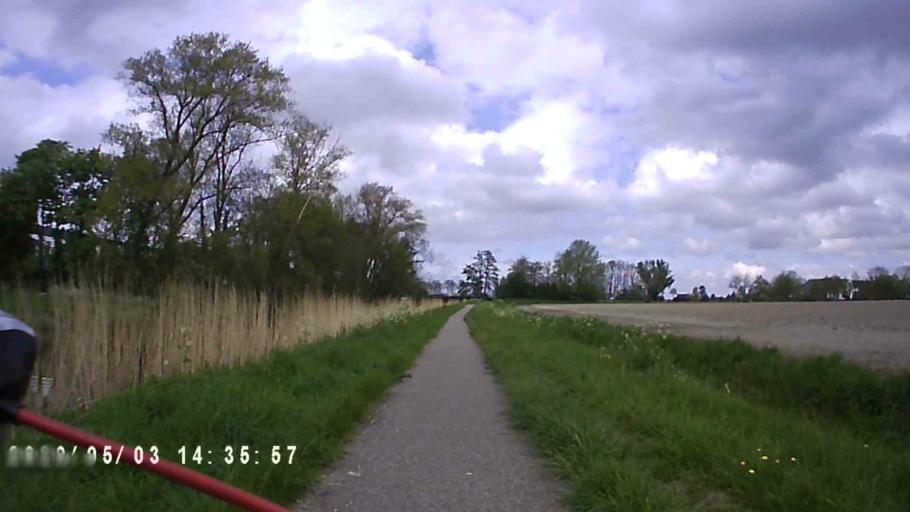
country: NL
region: Groningen
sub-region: Gemeente Zuidhorn
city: Oldehove
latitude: 53.3585
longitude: 6.3949
